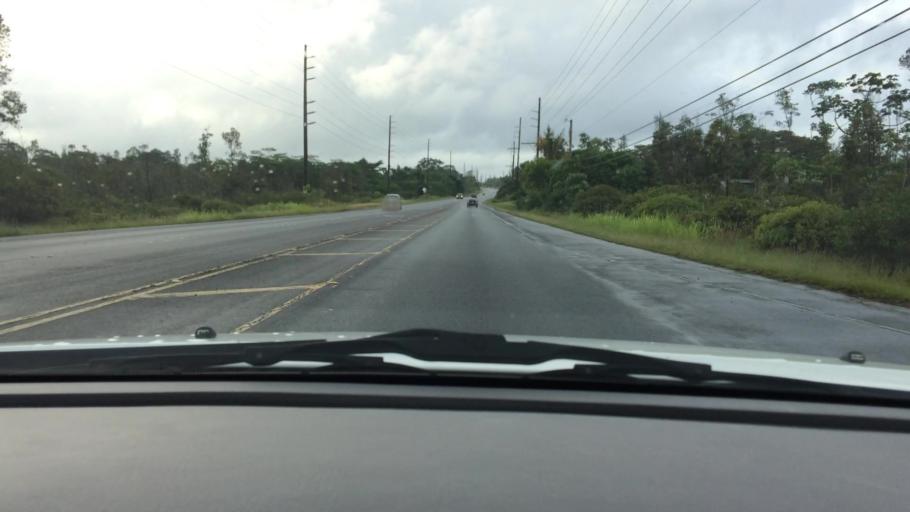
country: US
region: Hawaii
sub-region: Hawaii County
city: Ainaloa
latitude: 19.5533
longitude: -154.9856
